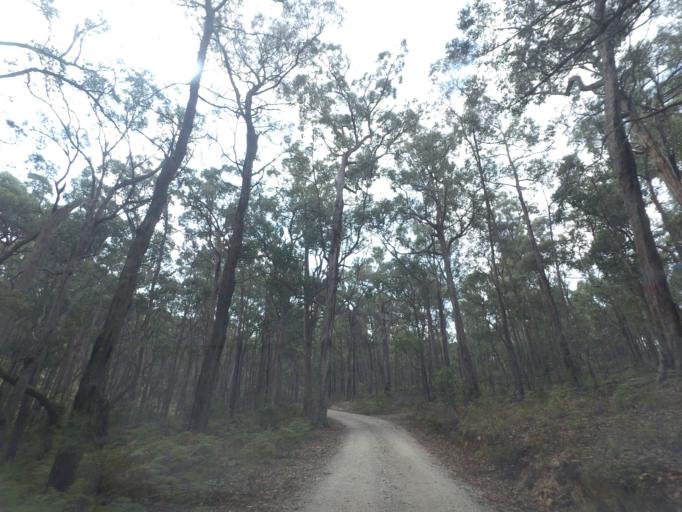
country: AU
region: Victoria
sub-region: Moorabool
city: Bacchus Marsh
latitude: -37.4620
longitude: 144.3621
